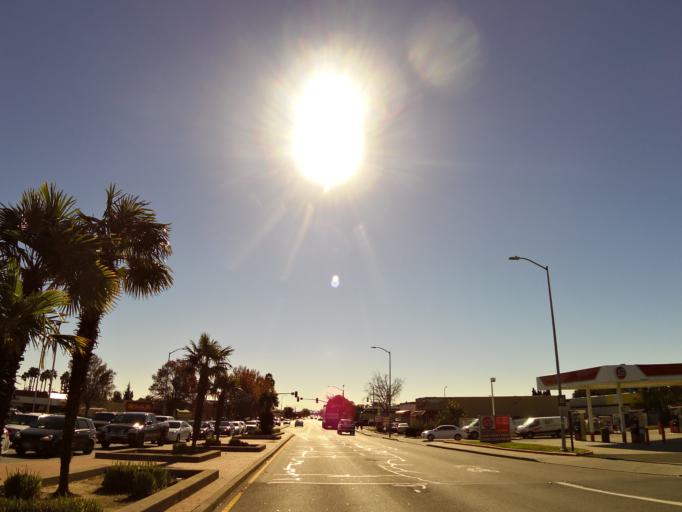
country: US
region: California
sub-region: Solano County
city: Fairfield
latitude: 38.2727
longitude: -122.0342
